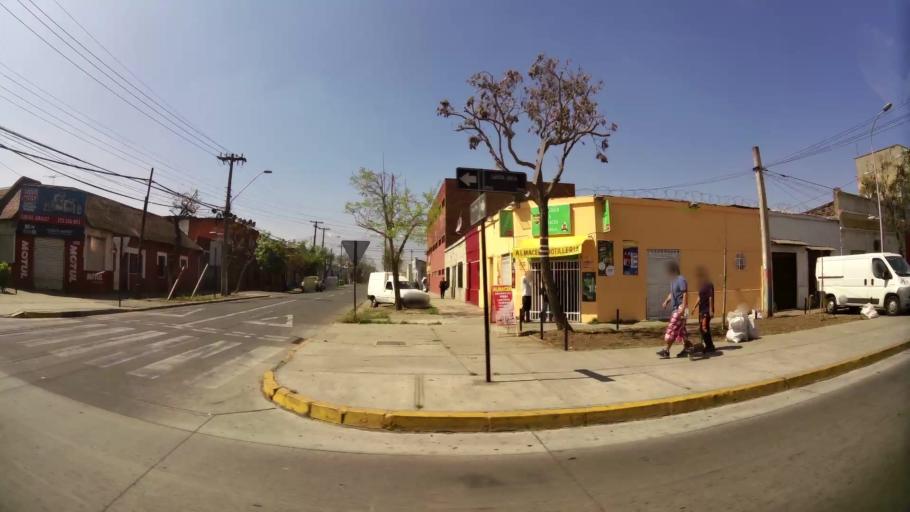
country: CL
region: Santiago Metropolitan
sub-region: Provincia de Santiago
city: Santiago
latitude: -33.4704
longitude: -70.6421
